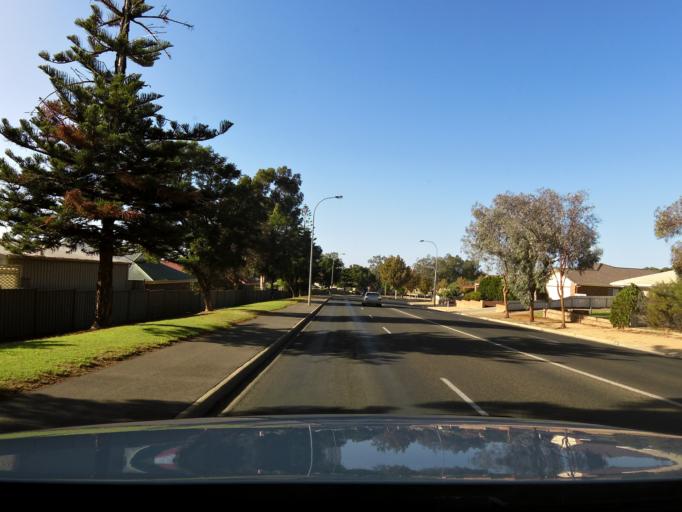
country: AU
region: South Australia
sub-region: Berri and Barmera
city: Berri
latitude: -34.2751
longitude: 140.6092
